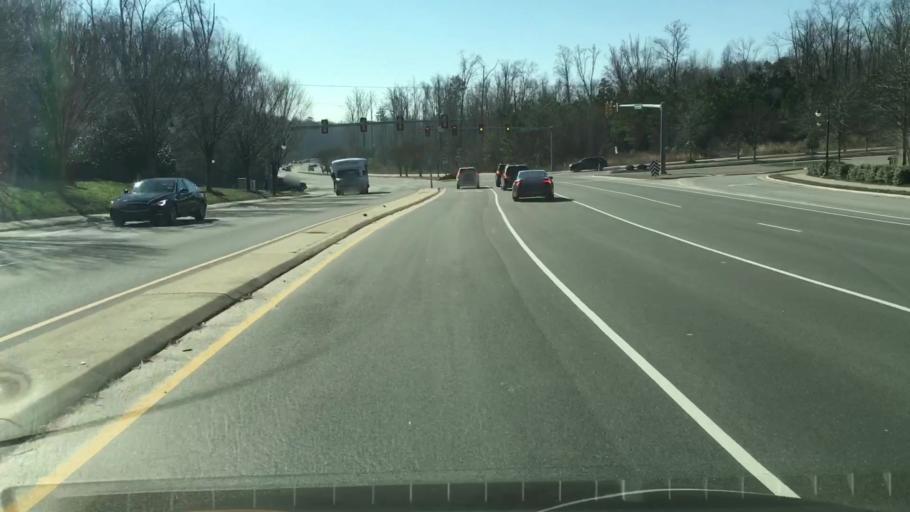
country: US
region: Virginia
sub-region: Chesterfield County
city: Brandermill
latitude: 37.5003
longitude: -77.6409
